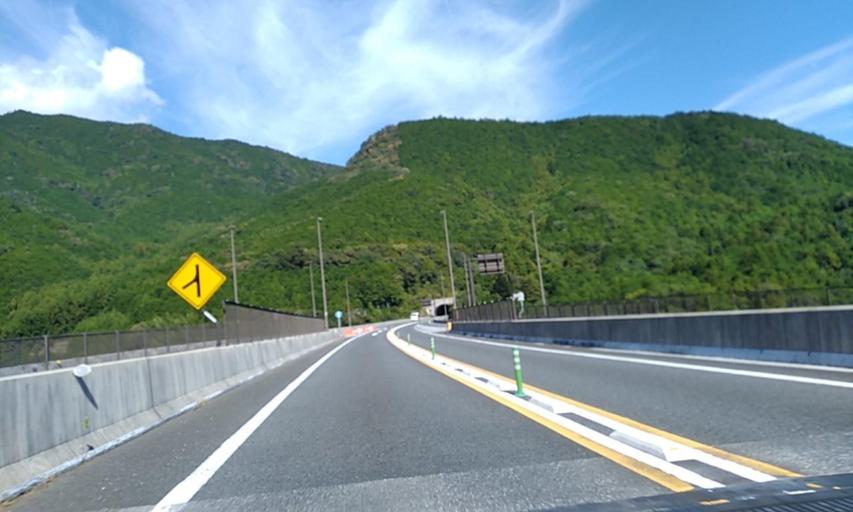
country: JP
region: Mie
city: Owase
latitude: 33.9323
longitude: 136.1386
